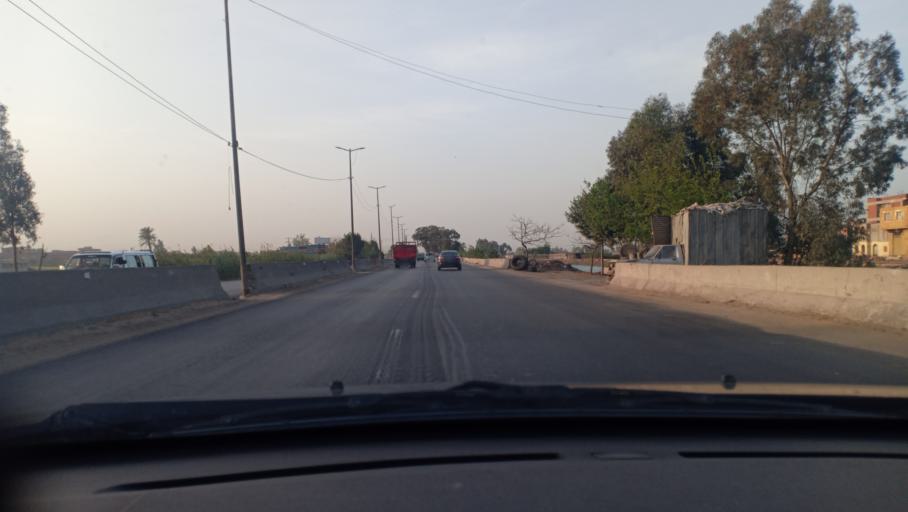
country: EG
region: Muhafazat al Minufiyah
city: Quwaysina
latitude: 30.5815
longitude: 31.2739
